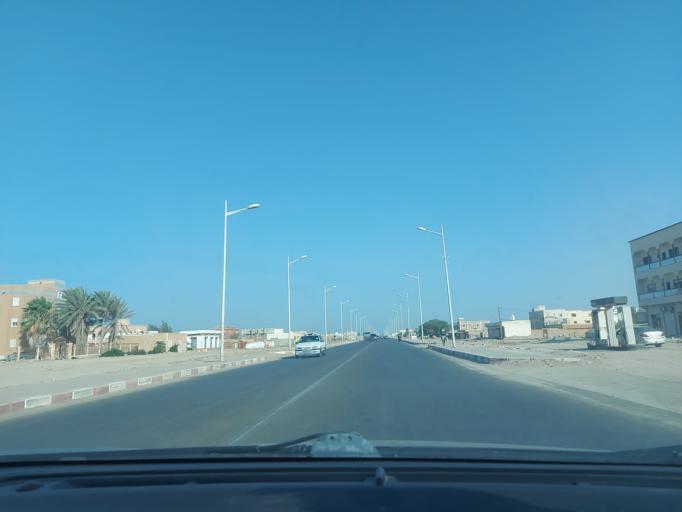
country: MR
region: Nouakchott
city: Nouakchott
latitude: 18.0896
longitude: -16.0074
